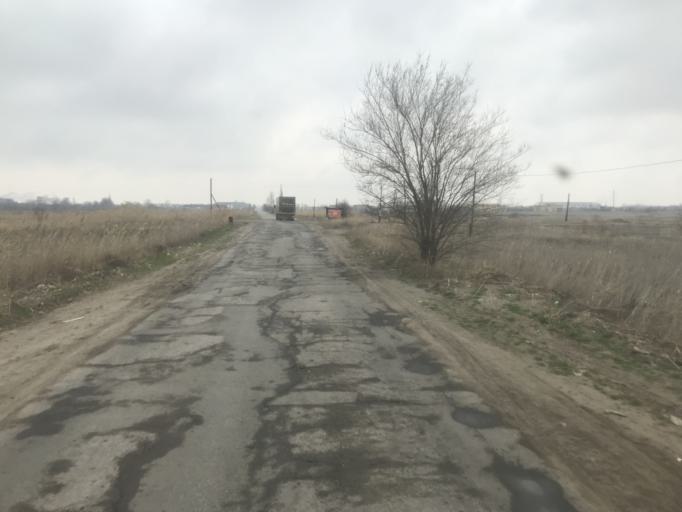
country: RU
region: Volgograd
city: Svetlyy Yar
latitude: 48.5185
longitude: 44.6271
